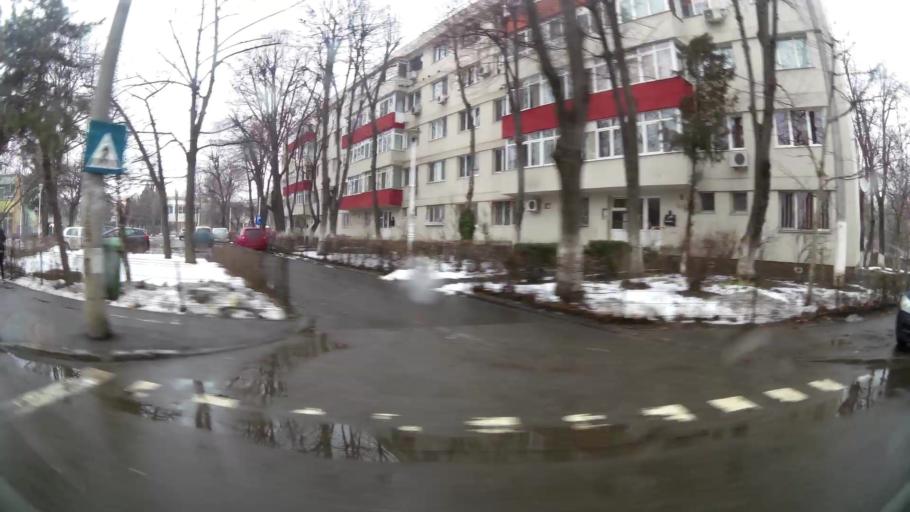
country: RO
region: Ilfov
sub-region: Comuna Chiajna
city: Rosu
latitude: 44.4828
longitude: 26.0542
